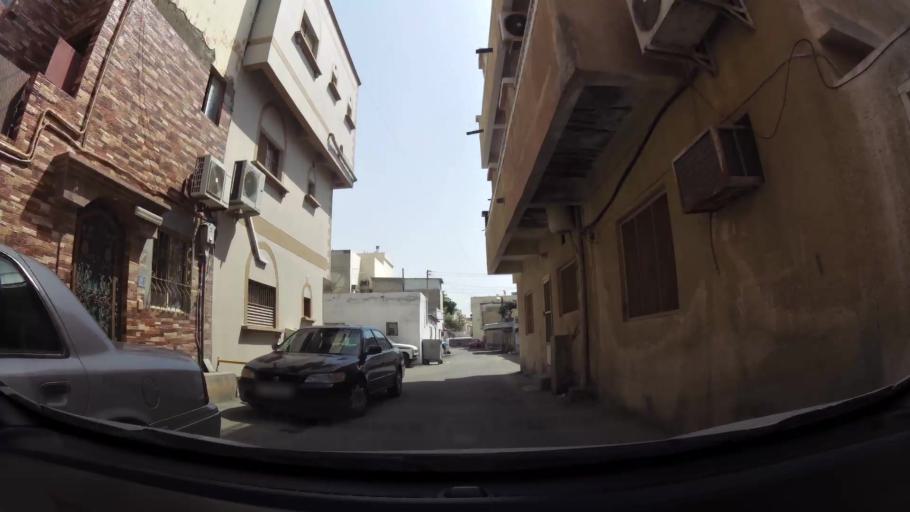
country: BH
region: Manama
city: Jidd Hafs
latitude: 26.2100
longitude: 50.4513
